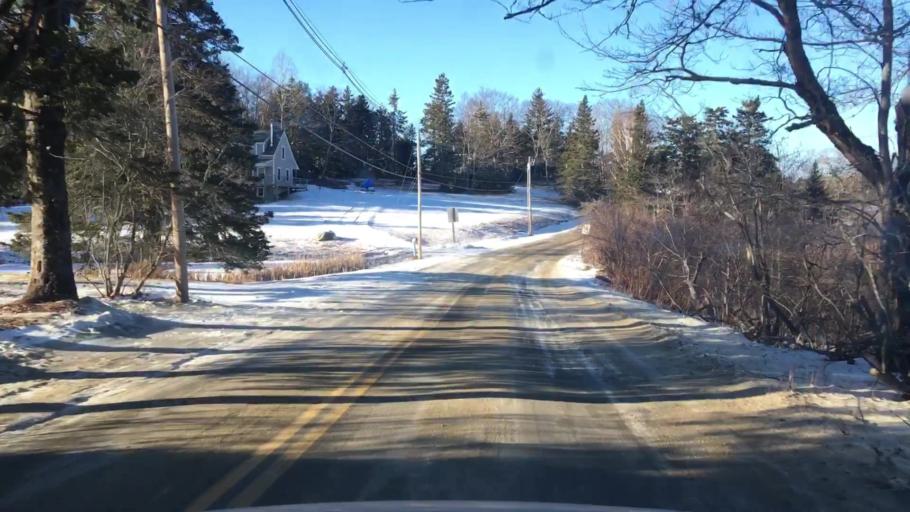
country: US
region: Maine
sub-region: Hancock County
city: Castine
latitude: 44.3472
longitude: -68.7469
